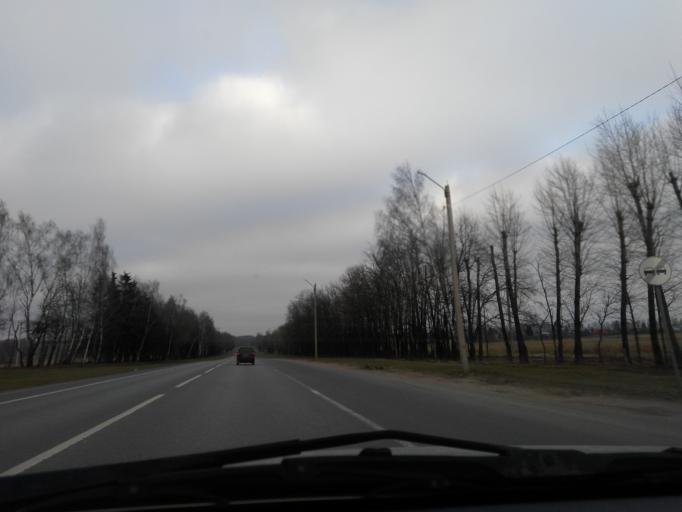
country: RU
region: Moskovskaya
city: Troitsk
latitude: 55.3295
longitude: 37.1656
